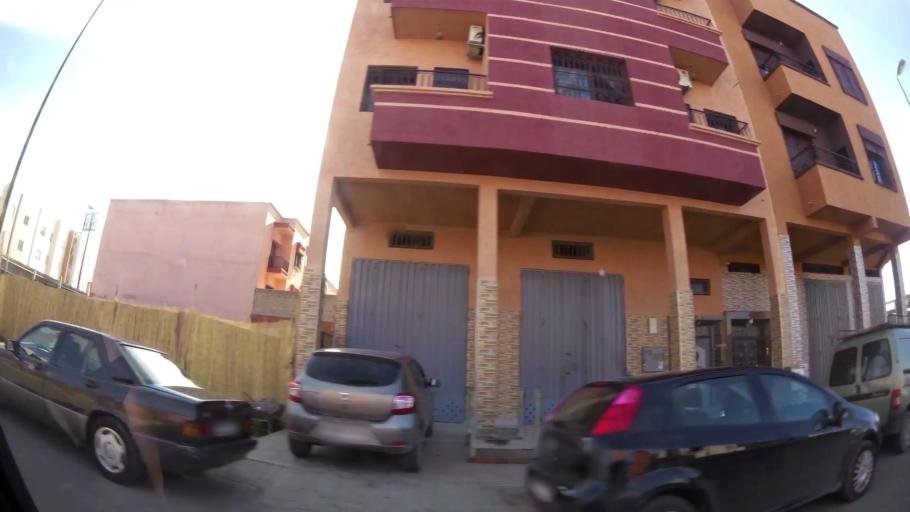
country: MA
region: Marrakech-Tensift-Al Haouz
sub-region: Marrakech
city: Marrakesh
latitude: 31.6802
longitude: -8.0464
